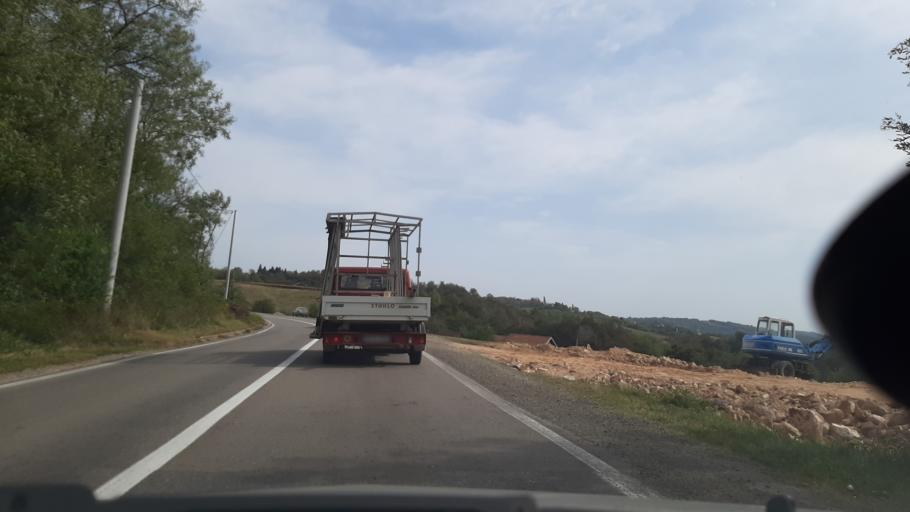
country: BA
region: Republika Srpska
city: Laktasi
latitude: 44.8672
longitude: 17.3437
